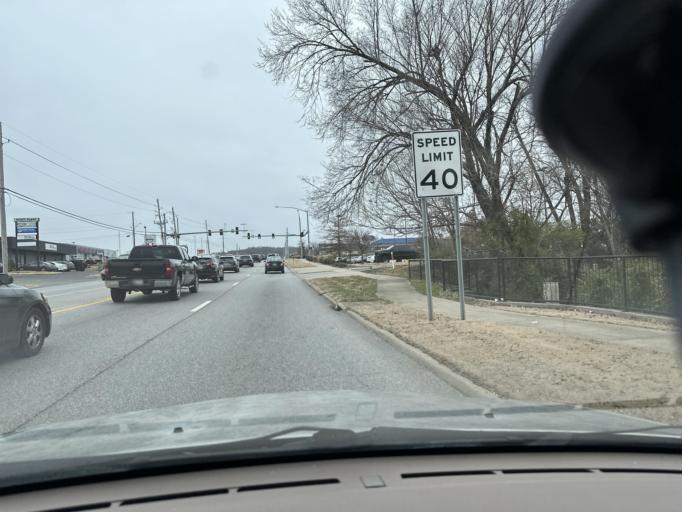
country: US
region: Arkansas
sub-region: Washington County
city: Johnson
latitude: 36.1142
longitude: -94.1451
